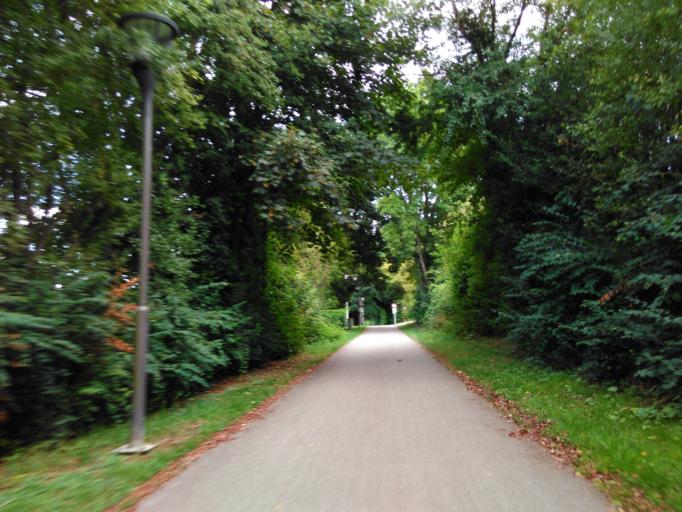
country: DE
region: Rheinland-Pfalz
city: Minden
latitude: 49.8179
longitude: 6.4747
